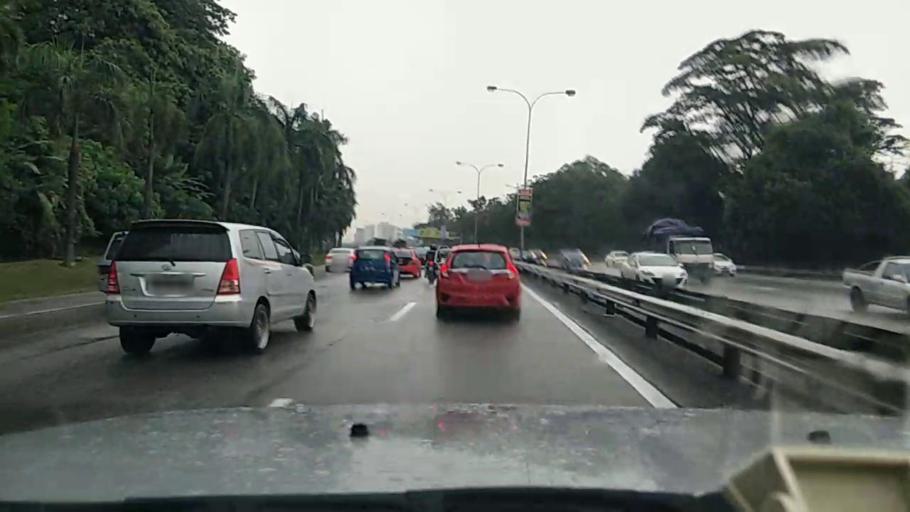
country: MY
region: Kuala Lumpur
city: Kuala Lumpur
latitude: 3.1077
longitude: 101.6922
